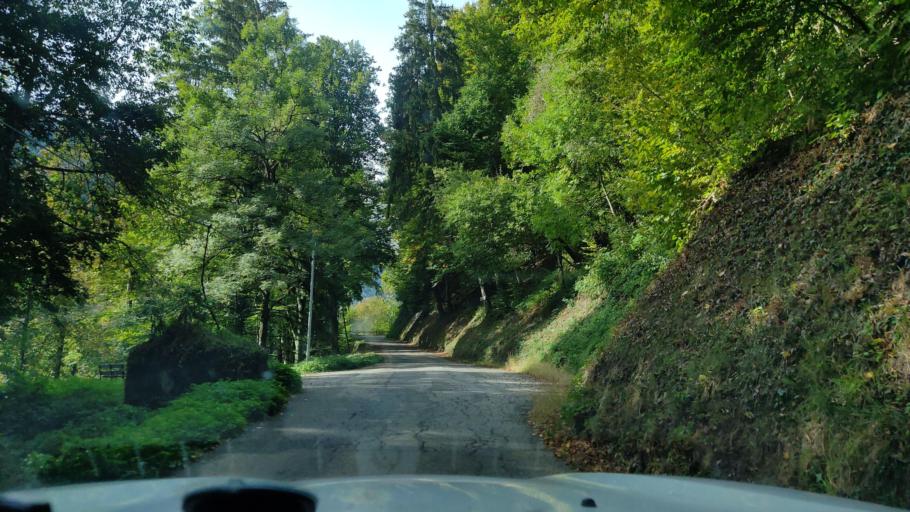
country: FR
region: Rhone-Alpes
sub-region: Departement de la Savoie
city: Beaufort
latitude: 45.7234
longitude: 6.5141
